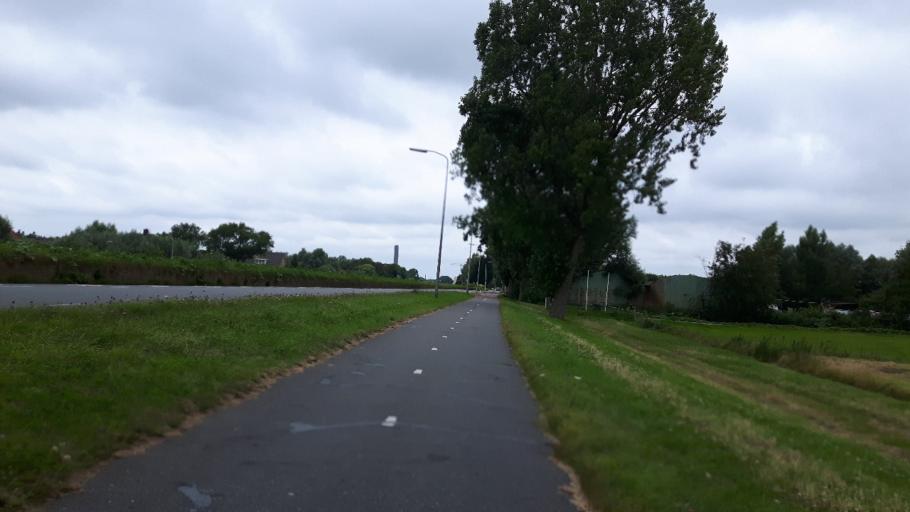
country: NL
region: South Holland
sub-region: Gemeente Delft
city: Delft
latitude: 51.9741
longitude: 4.3853
